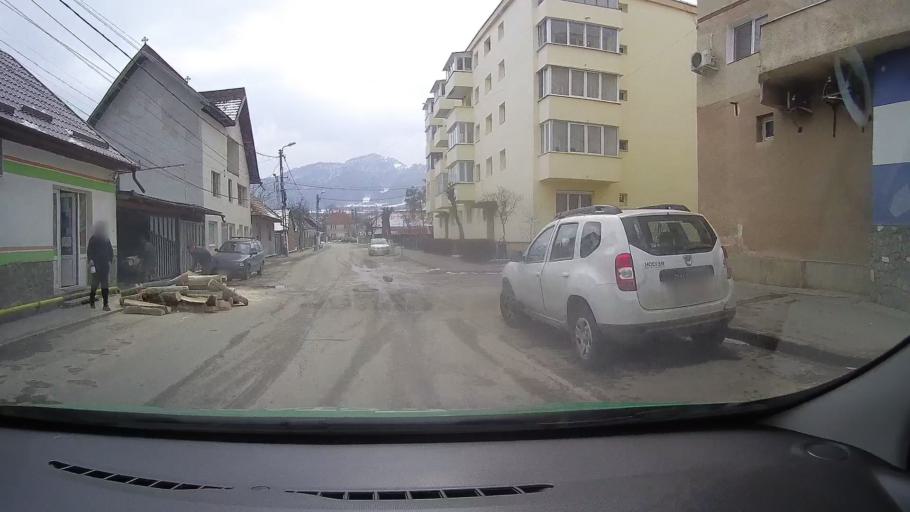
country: RO
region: Brasov
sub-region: Comuna Zarnesti
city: Zarnesti
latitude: 45.5587
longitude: 25.3243
